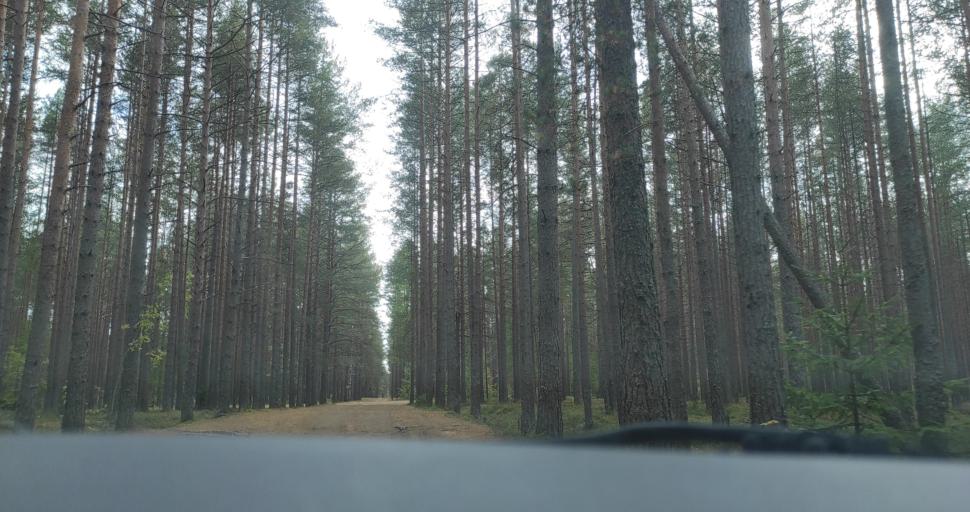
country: RU
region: Leningrad
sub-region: Vsevolzhskij Rajon
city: Vaskelovo
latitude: 60.4098
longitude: 30.3286
